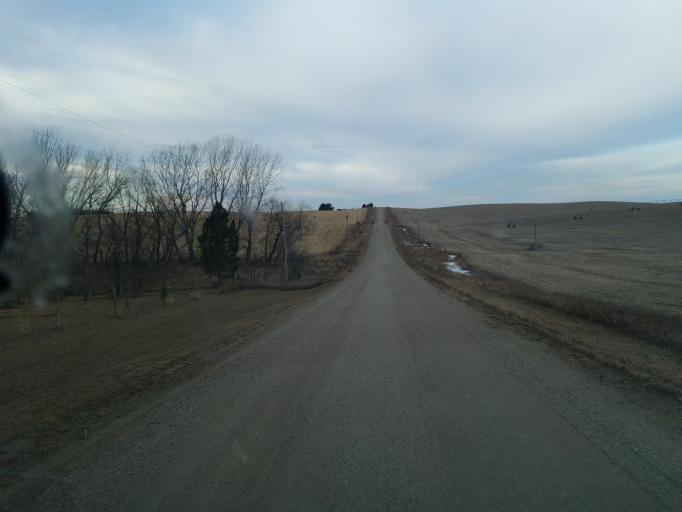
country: US
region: Nebraska
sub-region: Knox County
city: Bloomfield
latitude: 42.5833
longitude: -97.6317
